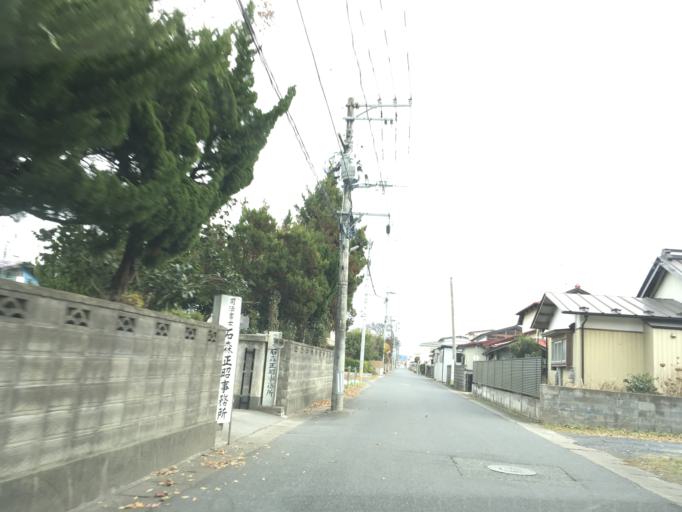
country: JP
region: Miyagi
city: Wakuya
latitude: 38.6922
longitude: 141.1990
